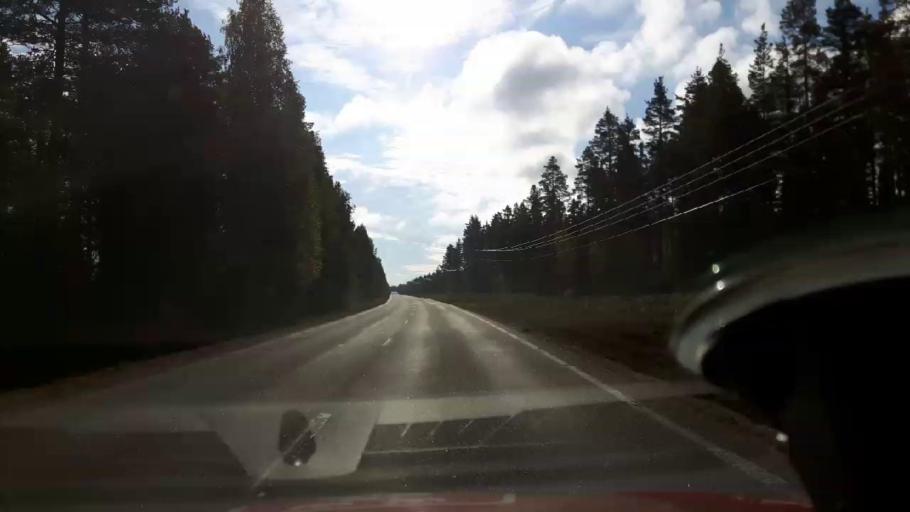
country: SE
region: Jaemtland
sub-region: Harjedalens Kommun
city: Sveg
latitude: 62.1017
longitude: 15.0711
